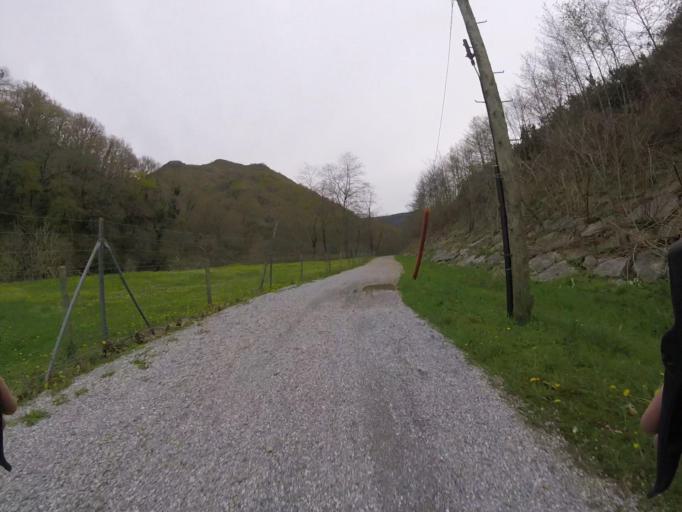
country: ES
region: Navarre
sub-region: Provincia de Navarra
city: Bera
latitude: 43.3060
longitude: -1.7348
